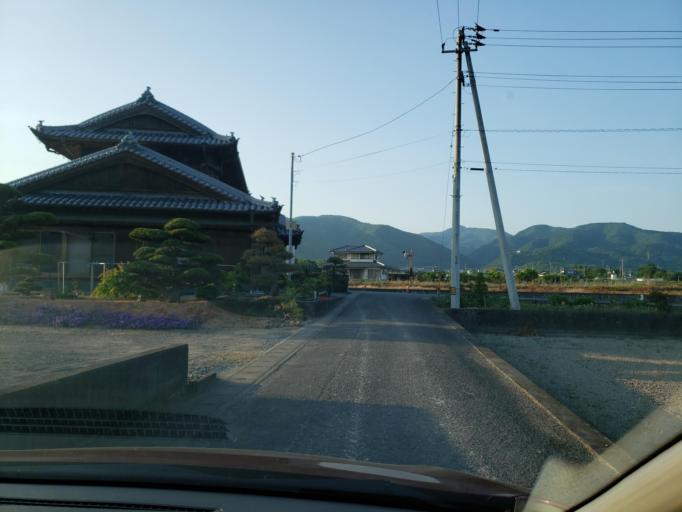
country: JP
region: Tokushima
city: Wakimachi
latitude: 34.0882
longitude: 134.2346
